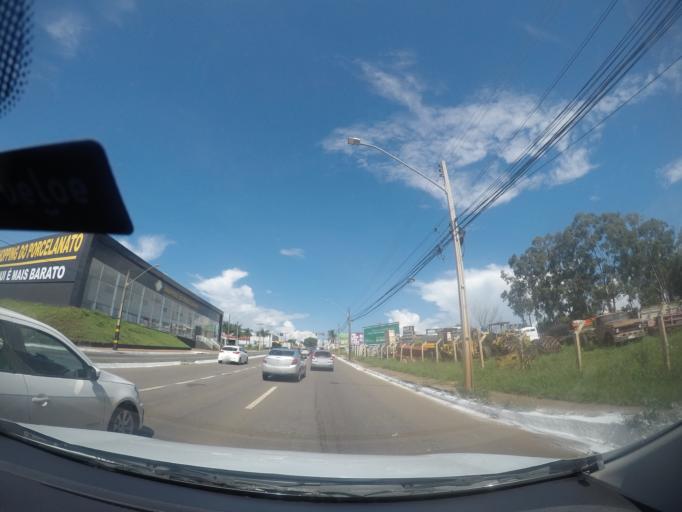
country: BR
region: Goias
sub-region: Goiania
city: Goiania
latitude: -16.6689
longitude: -49.3160
